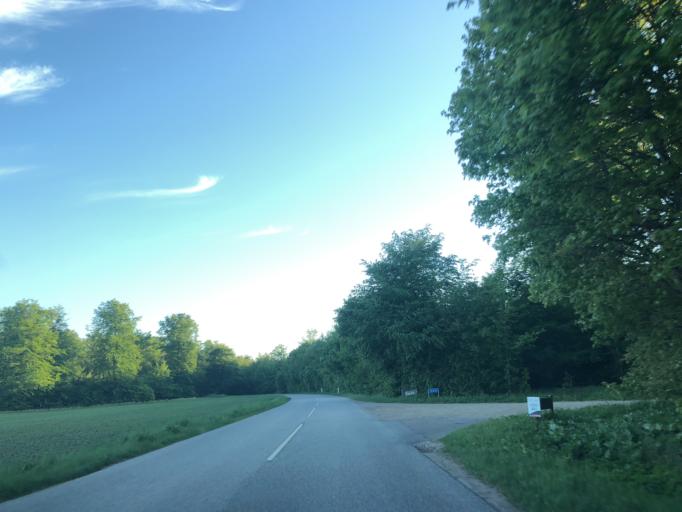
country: DK
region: Zealand
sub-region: Koge Kommune
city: Borup
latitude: 55.4355
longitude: 11.9417
